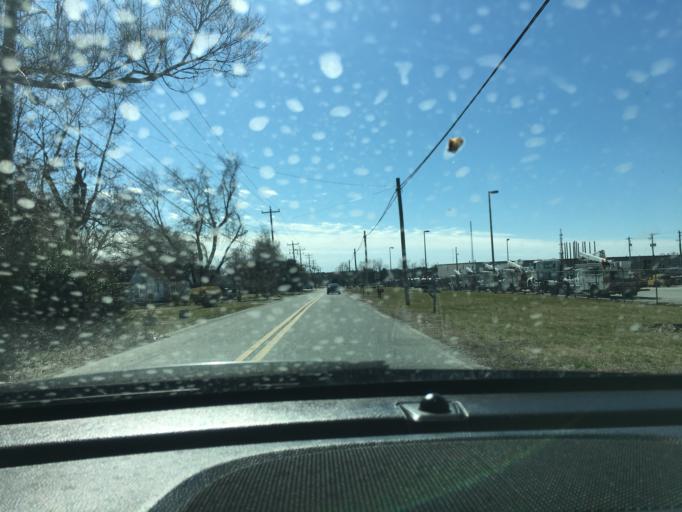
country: US
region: Maryland
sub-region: Wicomico County
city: Delmar
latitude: 38.4073
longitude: -75.5692
